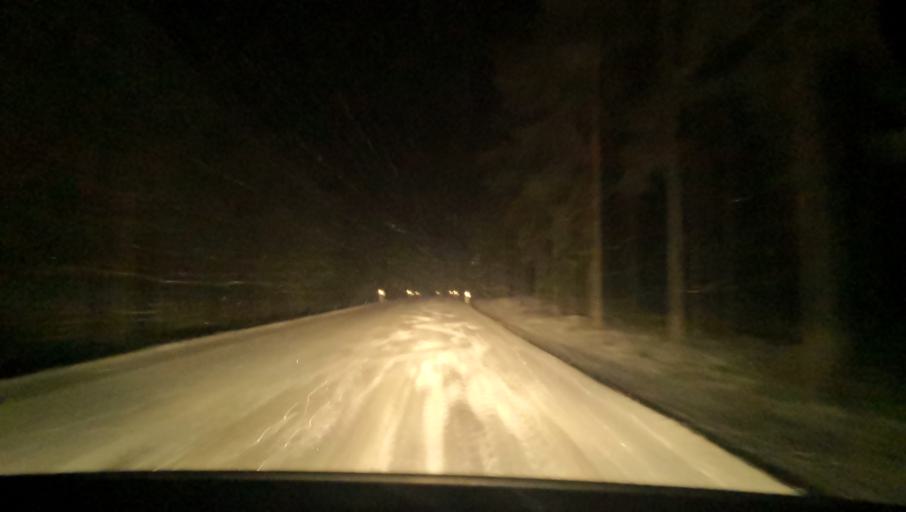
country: SE
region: Uppsala
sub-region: Heby Kommun
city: Tarnsjo
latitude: 60.1207
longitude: 16.8853
